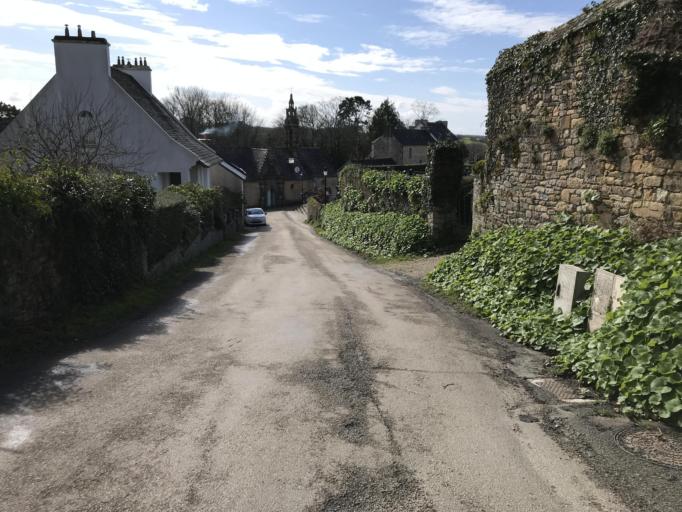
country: FR
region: Brittany
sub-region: Departement du Finistere
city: Daoulas
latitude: 48.3628
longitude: -4.2643
